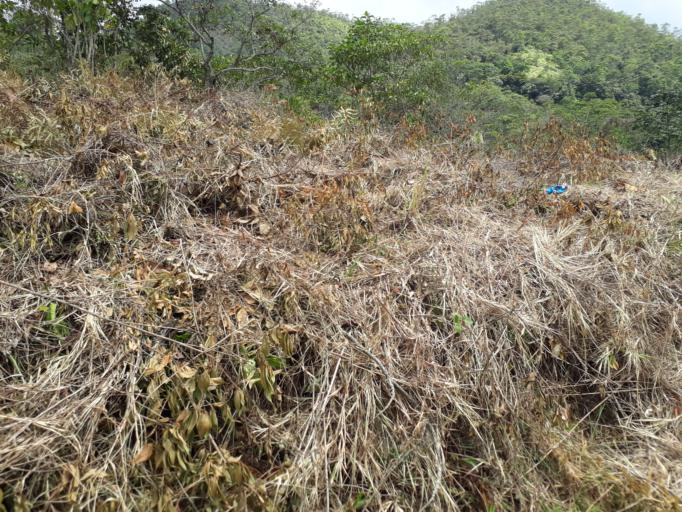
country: CO
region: Valle del Cauca
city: Cali
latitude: 3.3907
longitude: -76.6006
